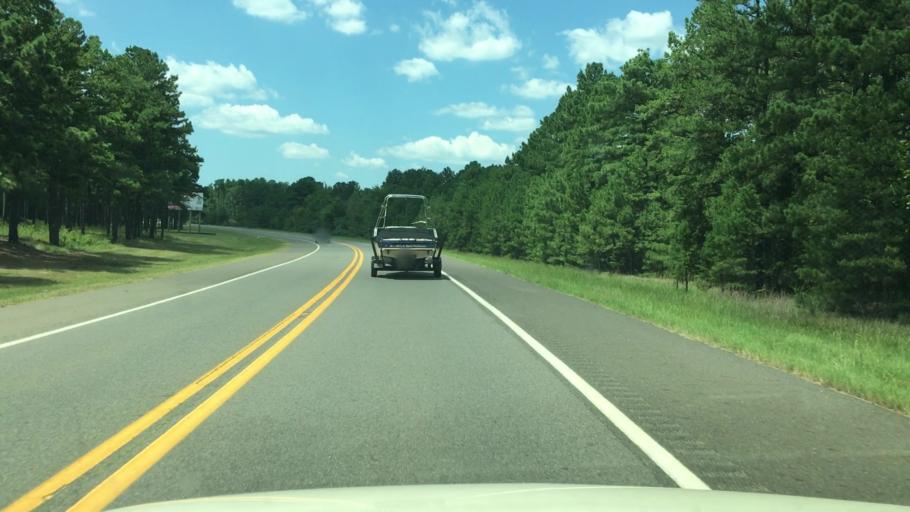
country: US
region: Arkansas
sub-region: Clark County
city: Arkadelphia
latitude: 34.2253
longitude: -93.0881
